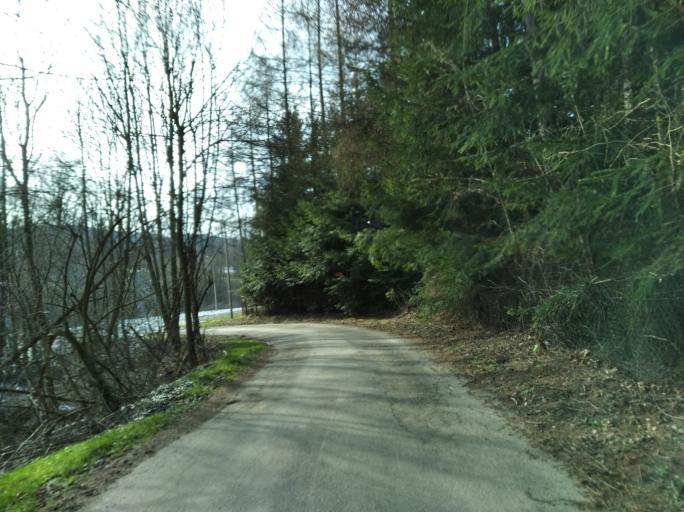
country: PL
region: Subcarpathian Voivodeship
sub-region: Powiat krosnienski
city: Korczyna
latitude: 49.7701
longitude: 21.7918
